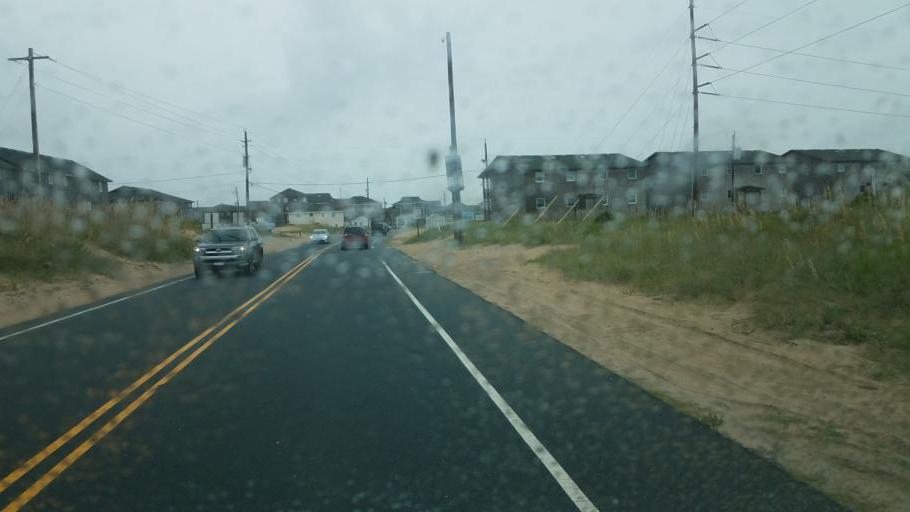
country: US
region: North Carolina
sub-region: Dare County
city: Buxton
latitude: 35.2685
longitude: -75.5188
